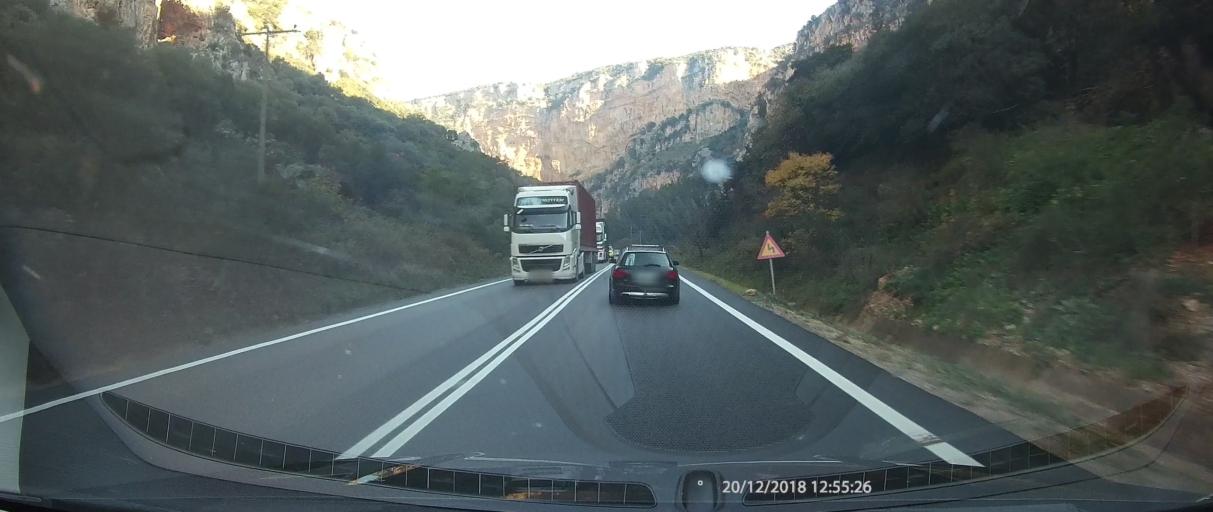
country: GR
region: West Greece
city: Aitoliko
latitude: 38.5006
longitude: 21.3712
